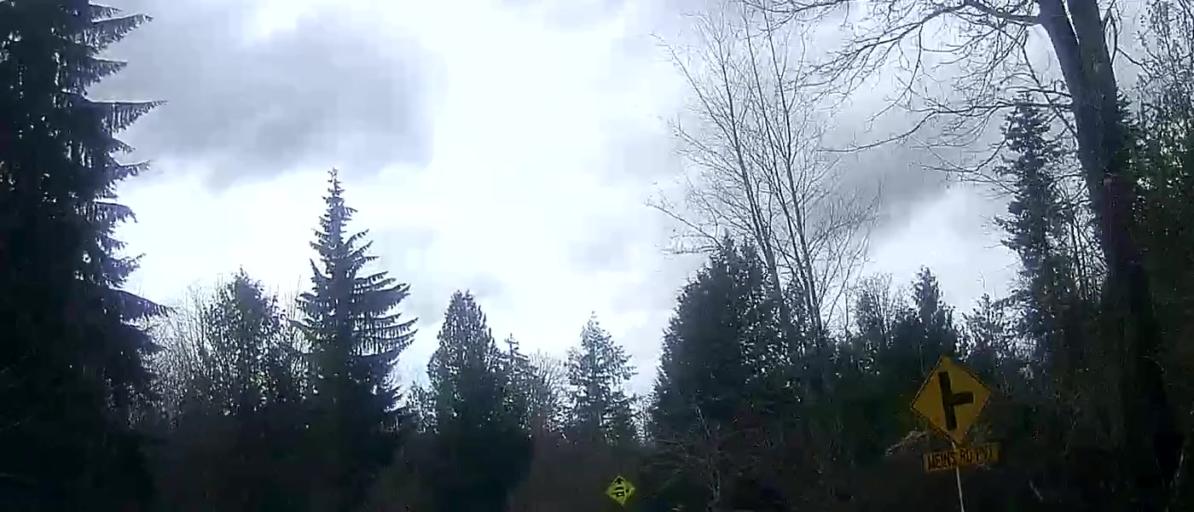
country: US
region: Washington
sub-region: Skagit County
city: Sedro-Woolley
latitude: 48.5800
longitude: -122.2495
